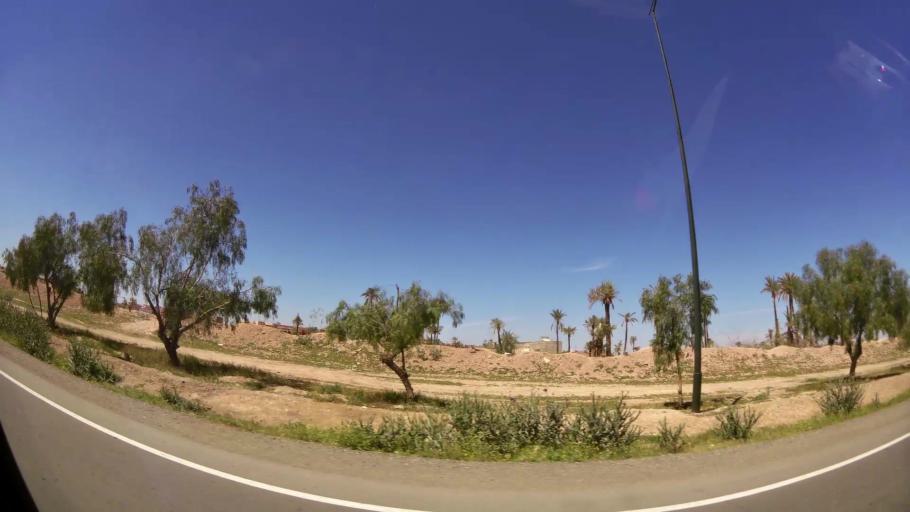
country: MA
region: Marrakech-Tensift-Al Haouz
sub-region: Marrakech
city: Marrakesh
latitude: 31.6677
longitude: -7.9904
